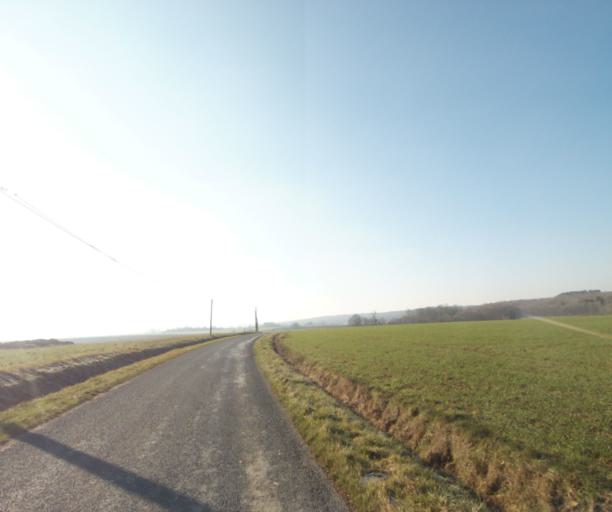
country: FR
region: Champagne-Ardenne
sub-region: Departement de la Haute-Marne
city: Bienville
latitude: 48.5329
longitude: 5.0094
